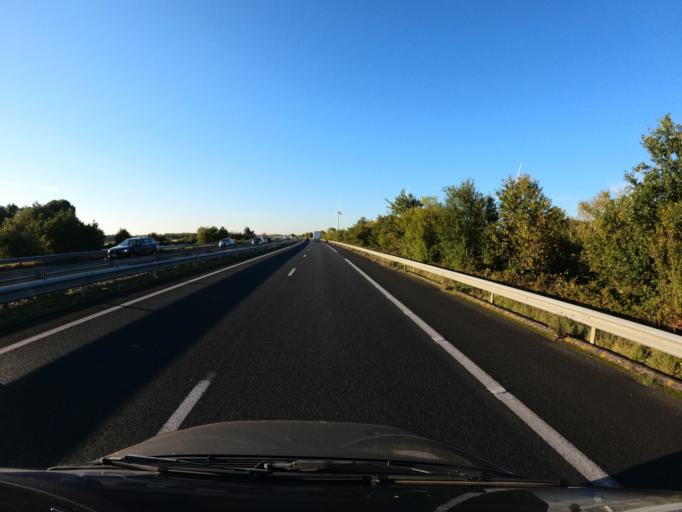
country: FR
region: Pays de la Loire
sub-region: Departement de la Vendee
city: Chauche
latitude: 46.8315
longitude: -1.2254
